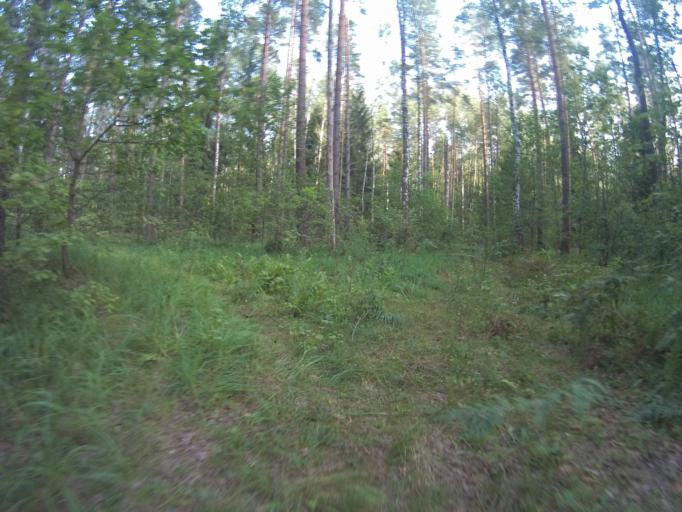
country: RU
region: Vladimir
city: Kommunar
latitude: 56.0809
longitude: 40.5072
